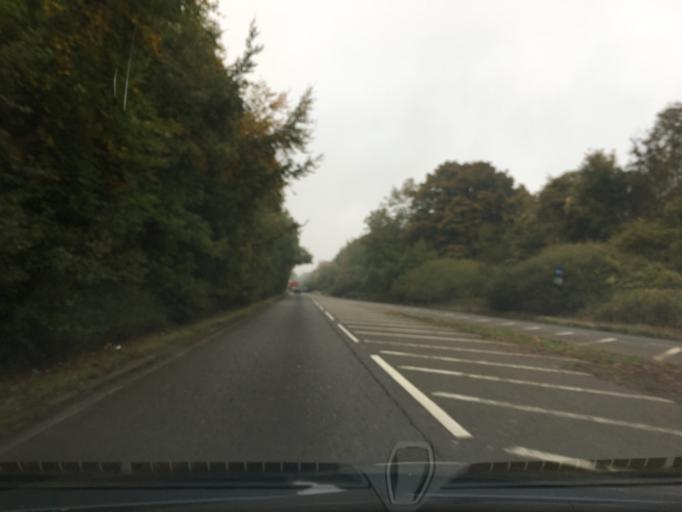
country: GB
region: England
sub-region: Surrey
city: Godalming
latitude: 51.2274
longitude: -0.6289
